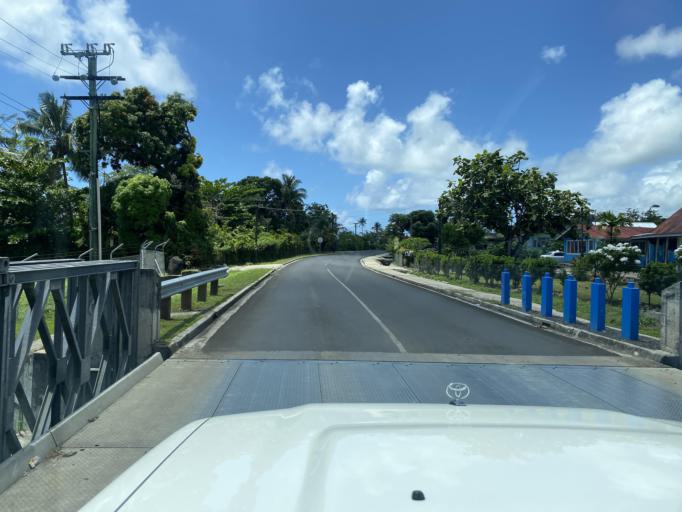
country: WS
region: Tuamasaga
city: Apia
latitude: -13.8394
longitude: -171.7587
